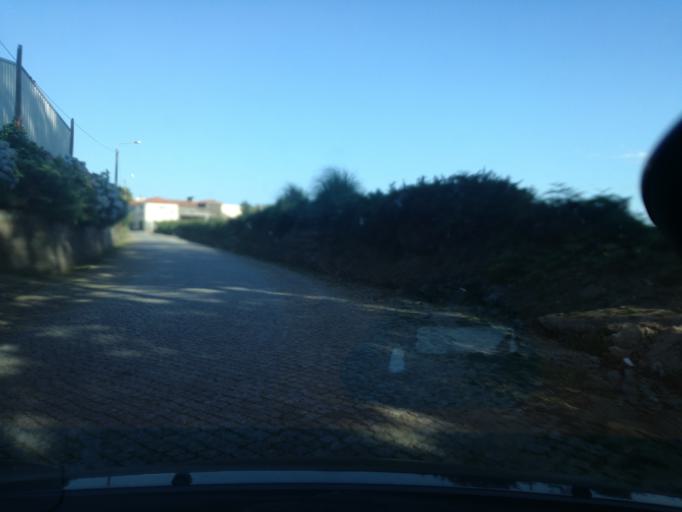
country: PT
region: Porto
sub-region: Matosinhos
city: Santa Cruz do Bispo
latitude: 41.2549
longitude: -8.6784
